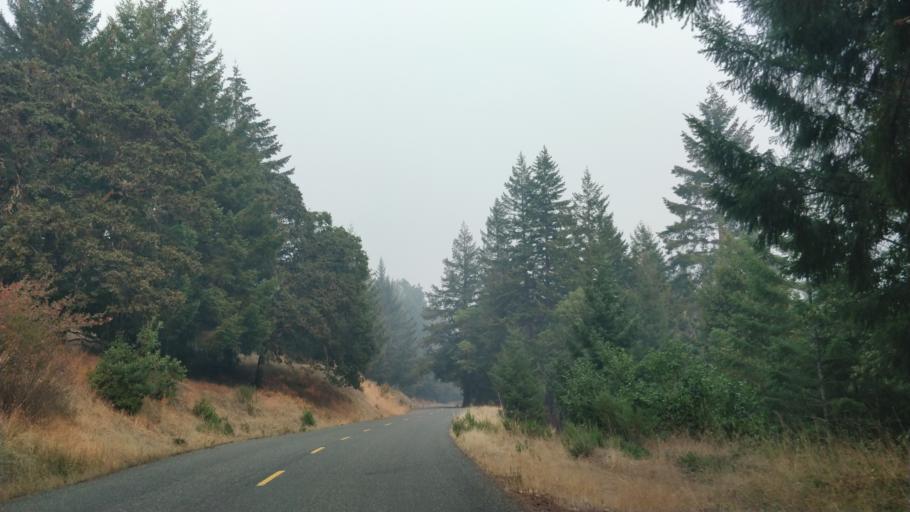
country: US
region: California
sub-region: Humboldt County
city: Rio Dell
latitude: 40.3291
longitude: -124.0398
